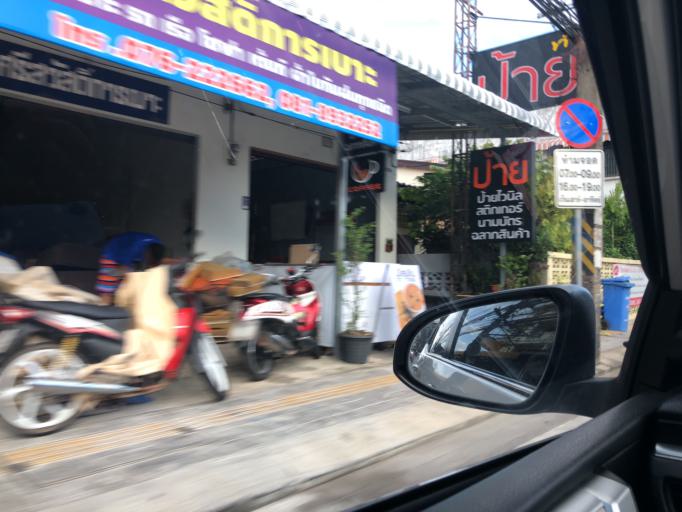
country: TH
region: Phuket
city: Wichit
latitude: 7.8960
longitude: 98.3894
